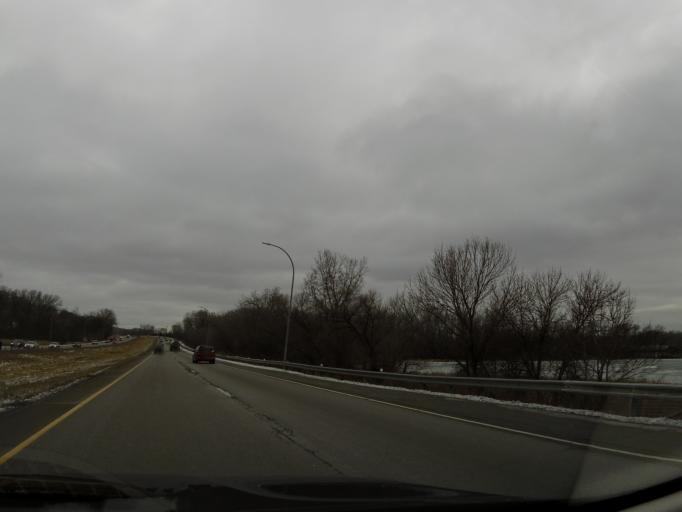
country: US
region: Minnesota
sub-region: Ramsey County
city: Maplewood
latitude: 44.9403
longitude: -93.0333
